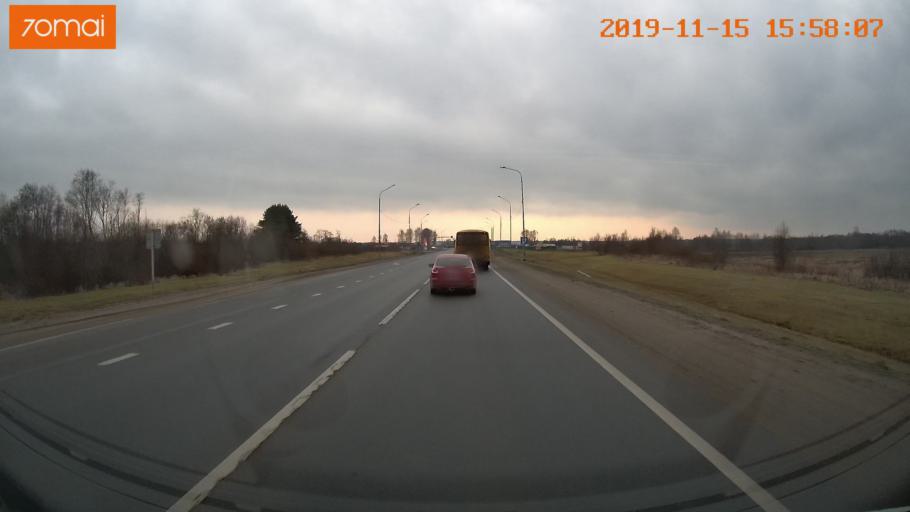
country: RU
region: Jaroslavl
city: Yaroslavl
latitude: 57.8236
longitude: 39.9577
